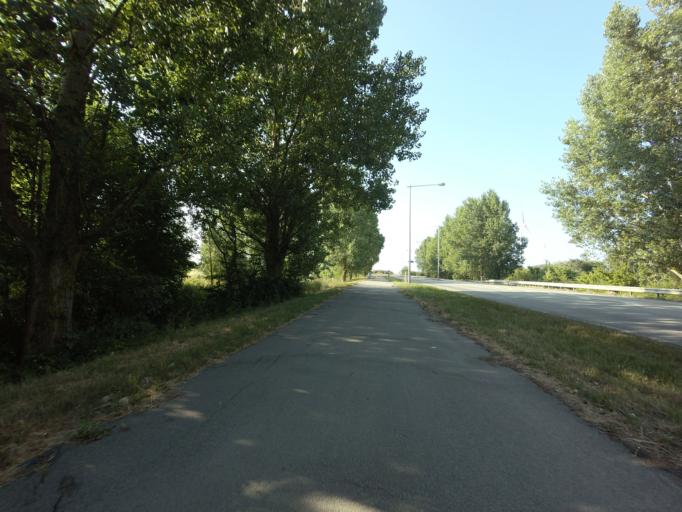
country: SE
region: Skane
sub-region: Landskrona
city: Landskrona
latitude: 55.8664
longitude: 12.8701
